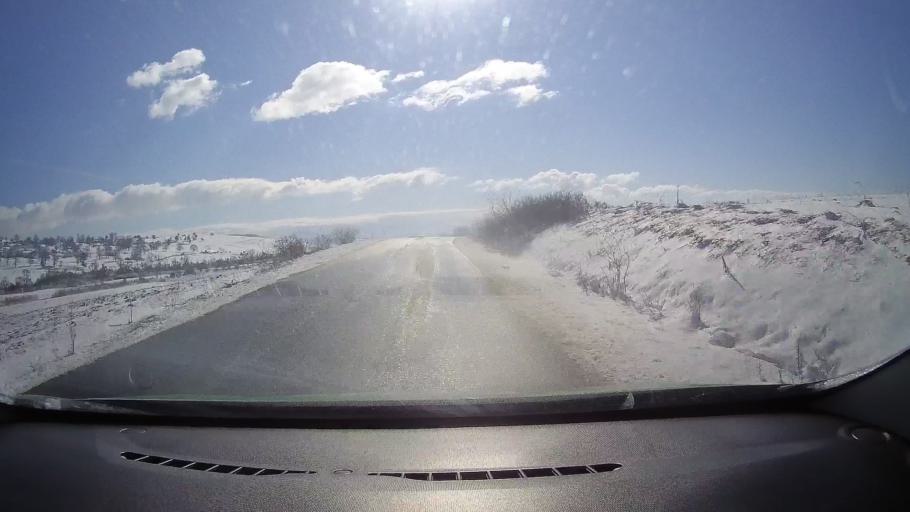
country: RO
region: Sibiu
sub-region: Comuna Rosia
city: Rosia
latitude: 45.8532
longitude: 24.3094
